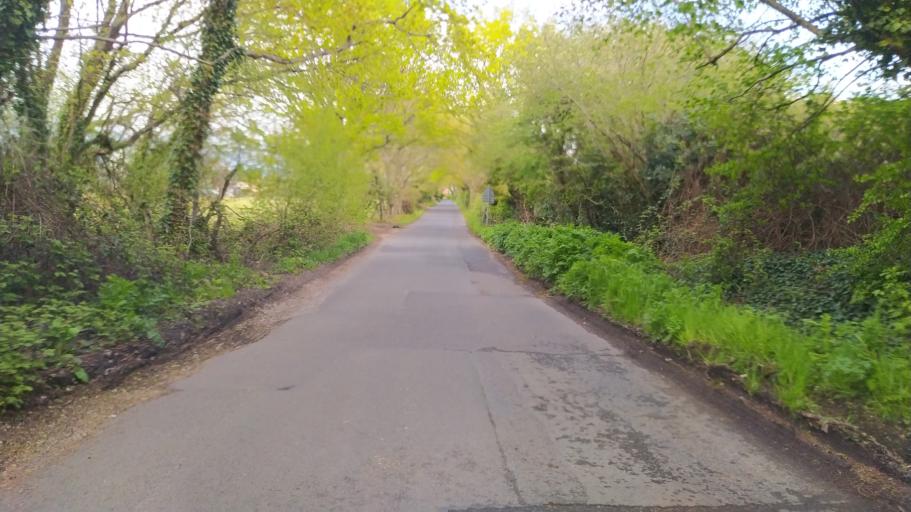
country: GB
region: England
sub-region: Hampshire
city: Bursledon
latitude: 50.8965
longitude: -1.3333
